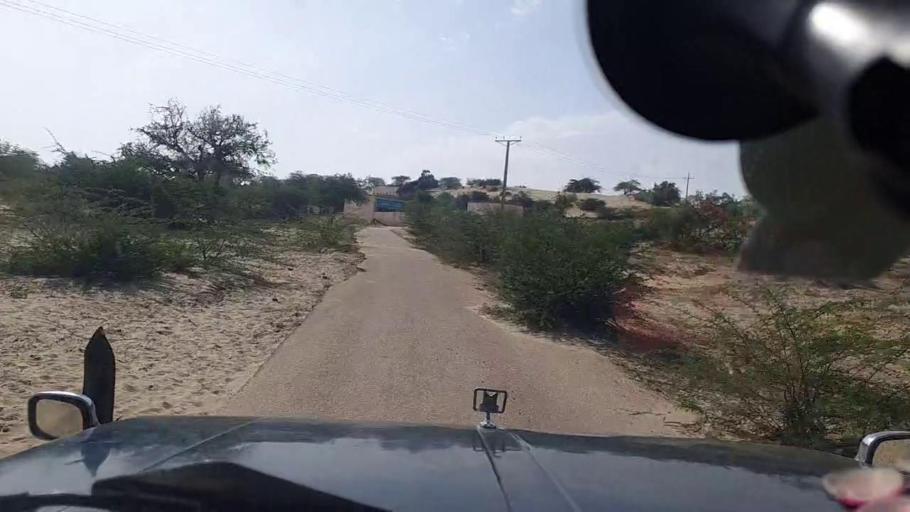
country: PK
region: Sindh
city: Diplo
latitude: 24.4176
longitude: 69.4599
